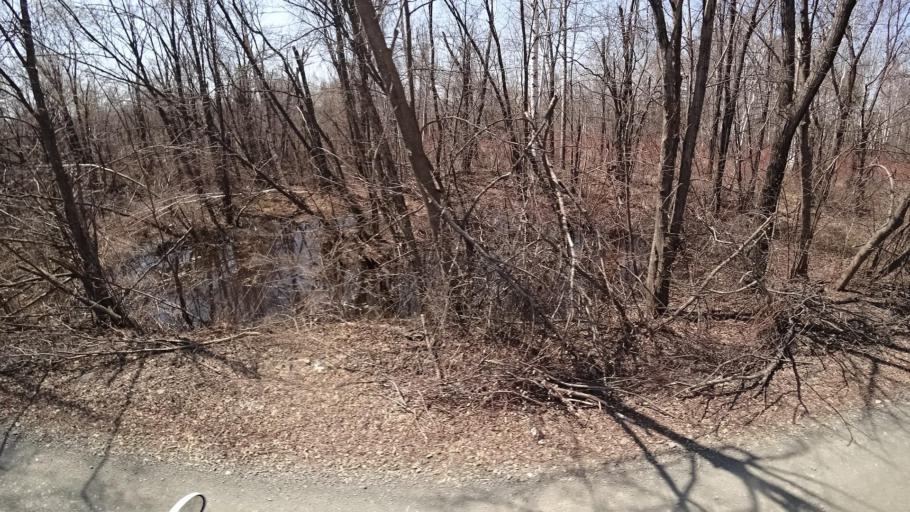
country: RU
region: Khabarovsk Krai
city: Khurba
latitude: 50.4197
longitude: 136.8328
